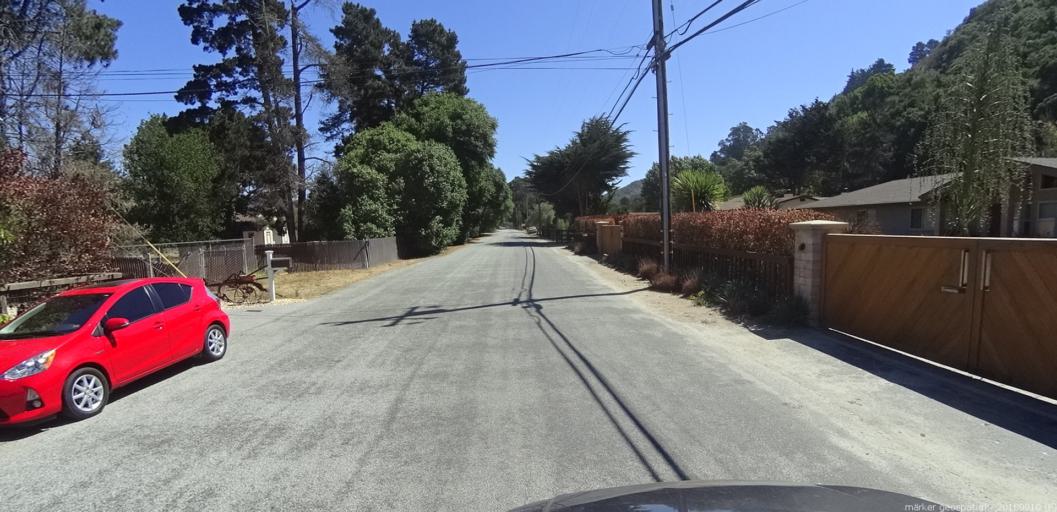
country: US
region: California
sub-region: Monterey County
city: Del Rey Oaks
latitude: 36.5256
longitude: -121.8363
